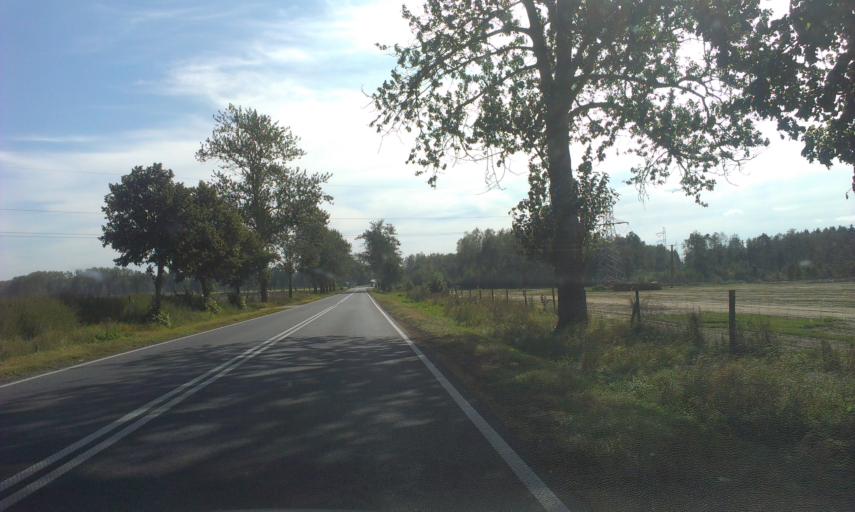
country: PL
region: West Pomeranian Voivodeship
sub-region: Powiat szczecinecki
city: Szczecinek
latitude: 53.6462
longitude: 16.7536
